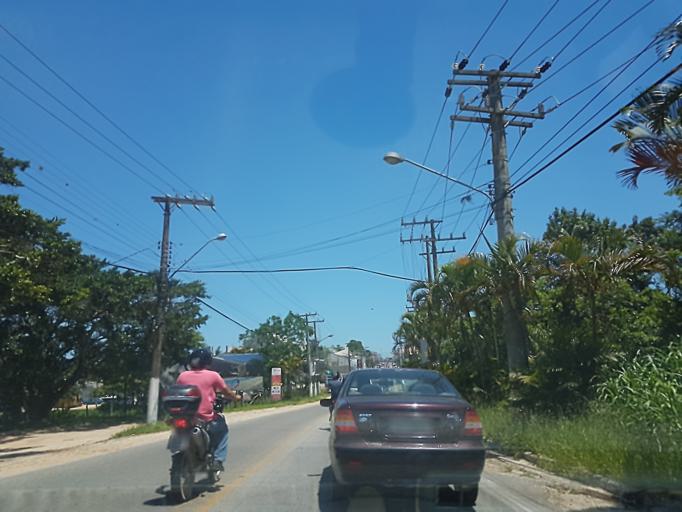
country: BR
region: Santa Catarina
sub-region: Jaguaruna
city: Jaguaruna
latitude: -28.6131
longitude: -49.0255
